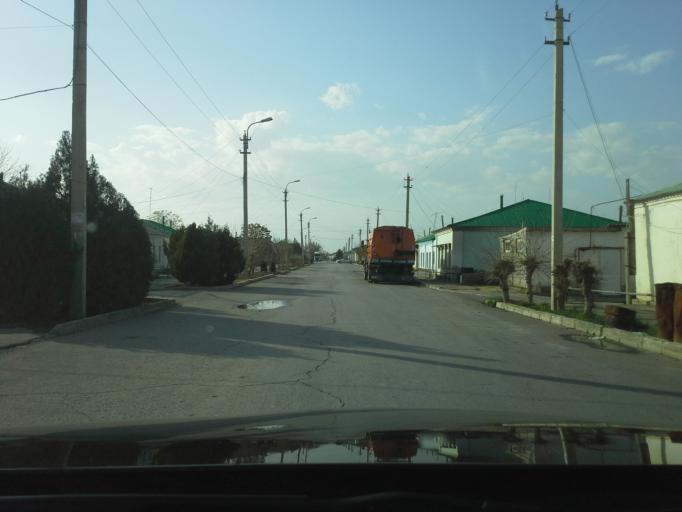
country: TM
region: Ahal
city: Abadan
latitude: 38.0235
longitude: 58.2359
